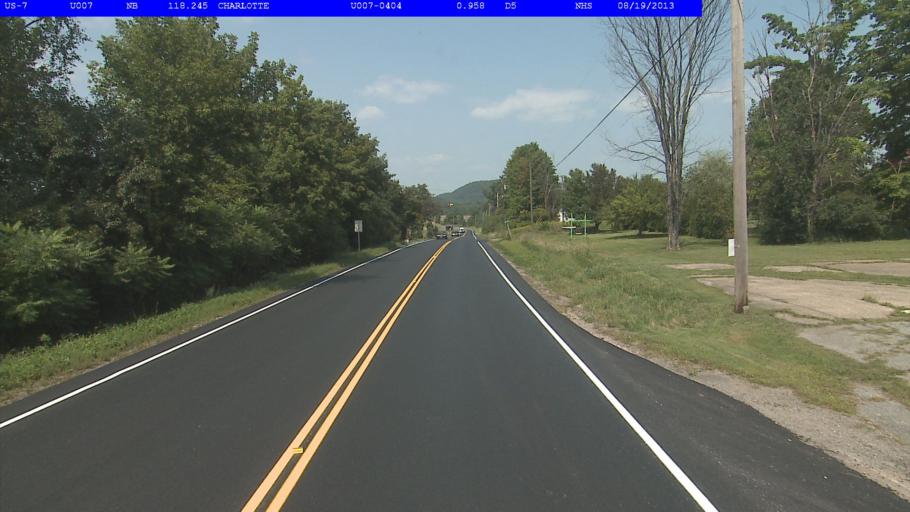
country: US
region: Vermont
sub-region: Addison County
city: Vergennes
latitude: 44.2760
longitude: -73.2347
